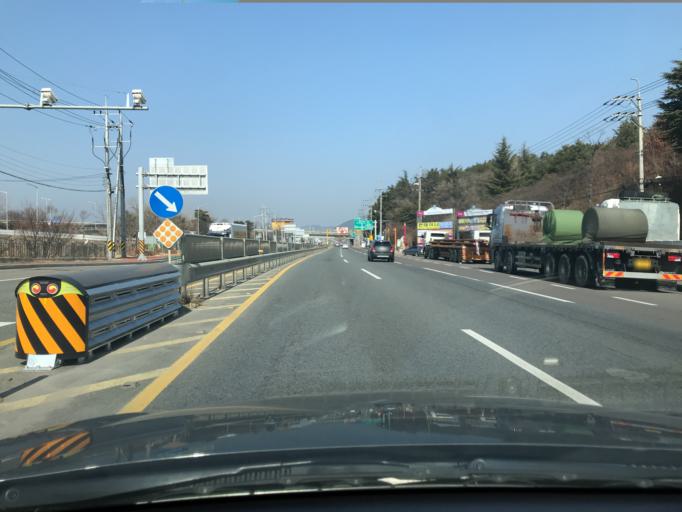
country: KR
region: Daegu
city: Hwawon
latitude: 35.7021
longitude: 128.4393
